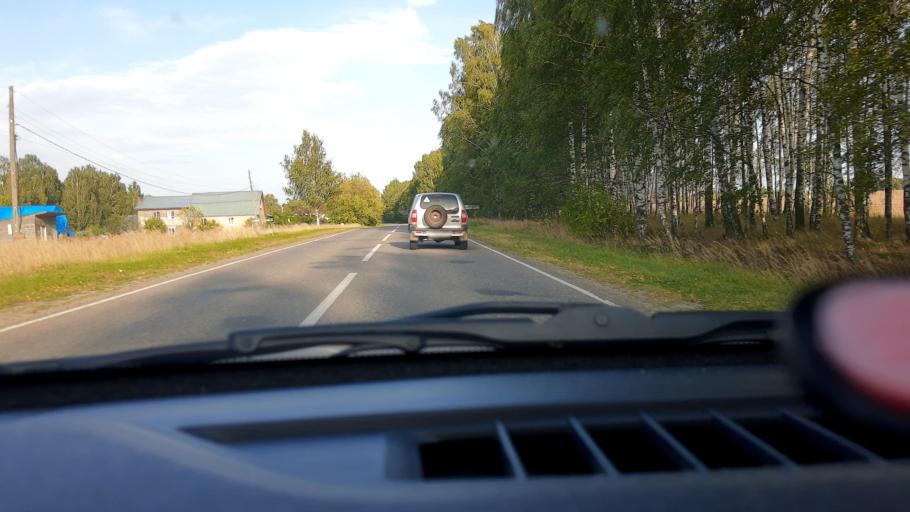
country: RU
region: Nizjnij Novgorod
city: Gorodets
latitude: 56.6677
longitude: 43.6139
